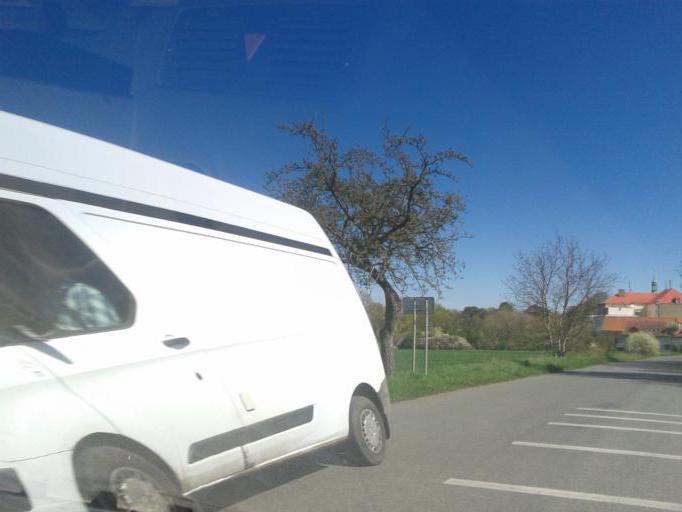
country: CZ
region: Central Bohemia
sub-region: Okres Beroun
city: Lodenice
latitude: 49.9060
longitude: 14.1443
